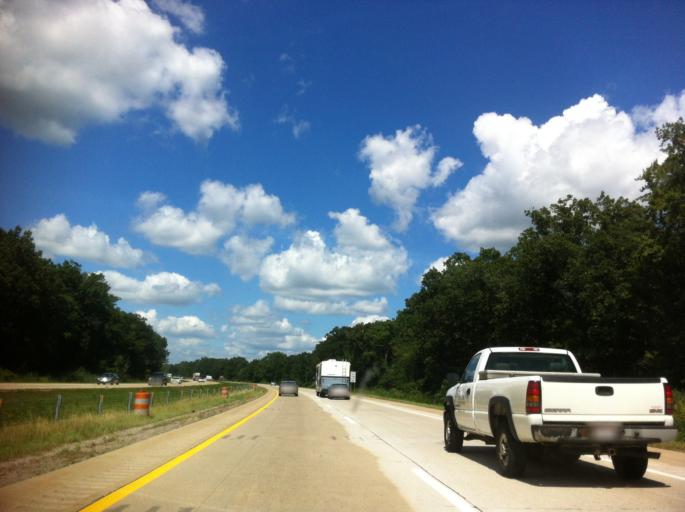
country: US
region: Michigan
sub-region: Monroe County
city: Petersburg
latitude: 41.8512
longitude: -83.6627
